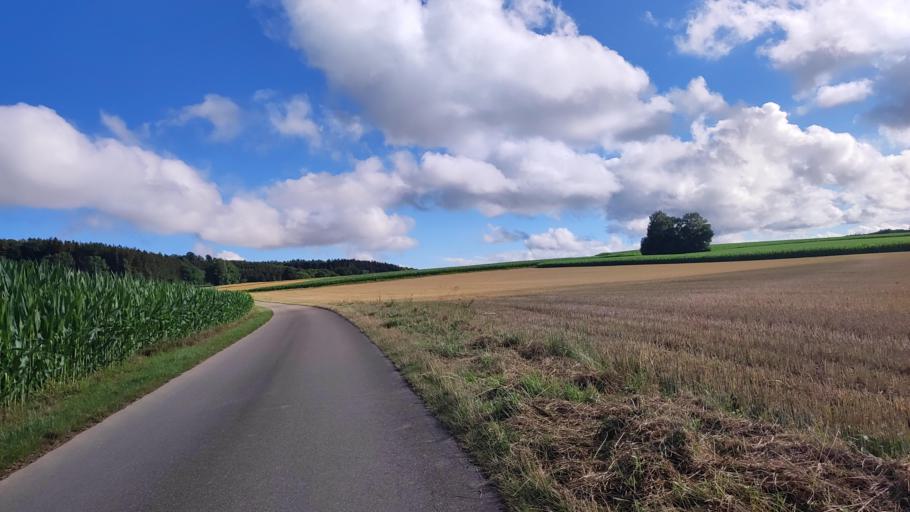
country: DE
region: Bavaria
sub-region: Swabia
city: Zusmarshausen
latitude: 48.3856
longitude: 10.5899
